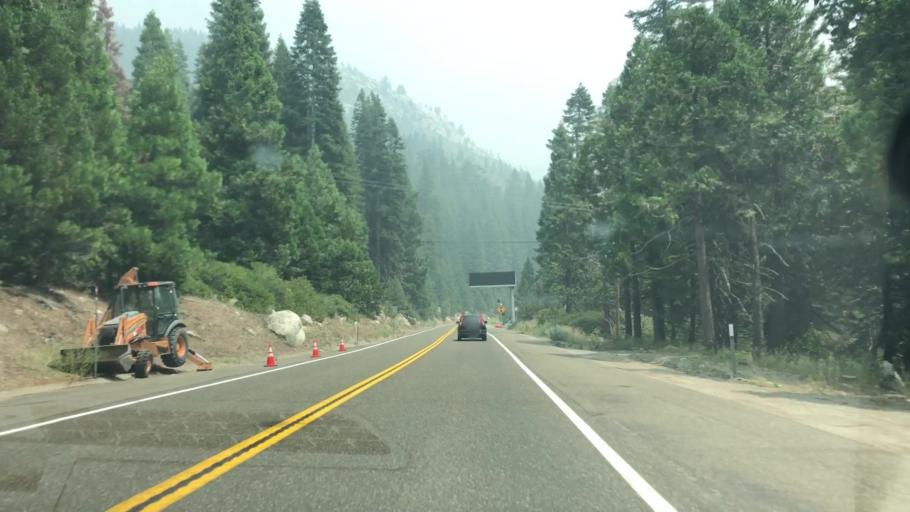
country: US
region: California
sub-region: El Dorado County
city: South Lake Tahoe
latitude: 38.8070
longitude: -120.1382
